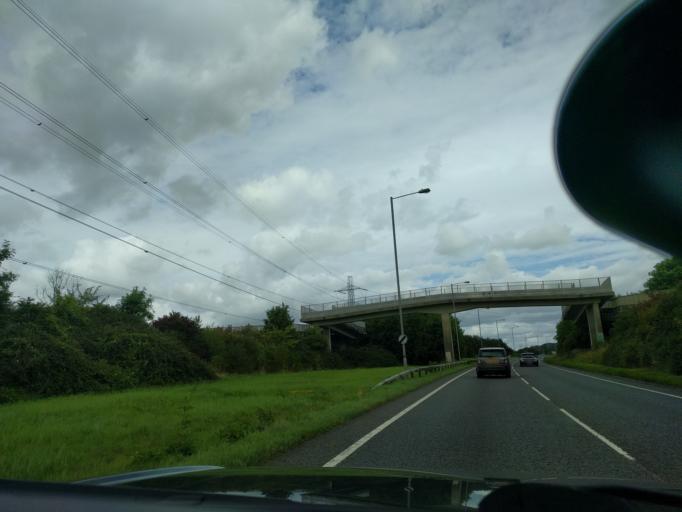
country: GB
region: England
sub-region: Wiltshire
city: Chippenham
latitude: 51.4623
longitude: -2.1502
